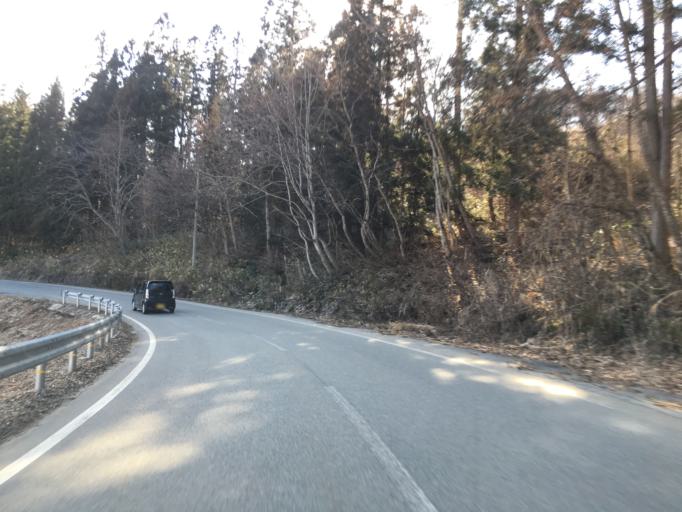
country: JP
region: Yamagata
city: Nagai
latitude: 37.9800
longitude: 140.0002
